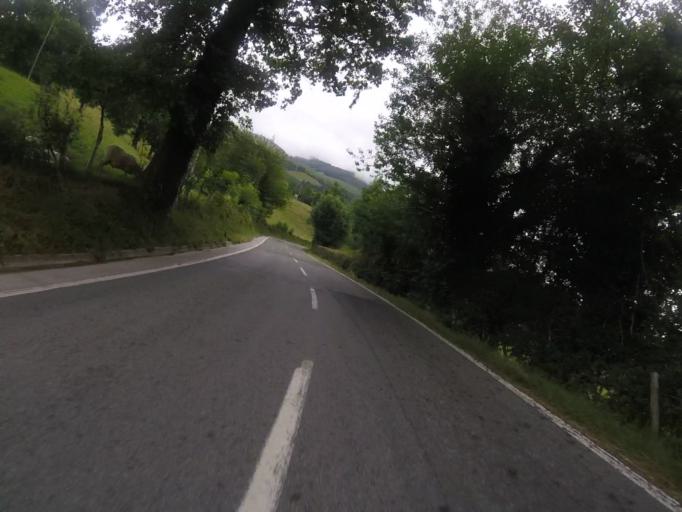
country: ES
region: Navarre
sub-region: Provincia de Navarra
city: Ezkurra
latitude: 43.0828
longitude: -1.8363
